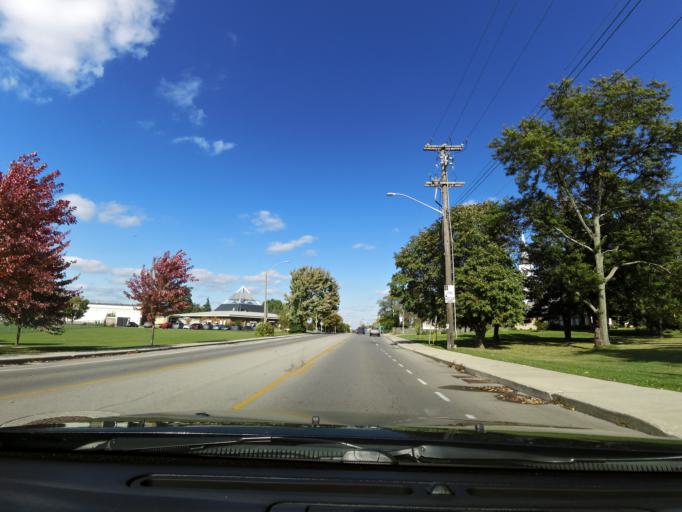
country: CA
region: Ontario
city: Hamilton
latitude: 43.2314
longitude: -79.9125
